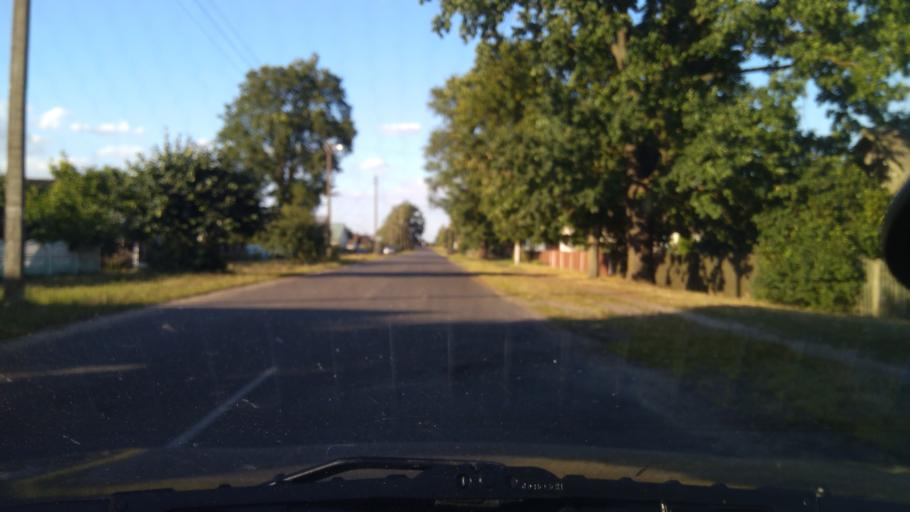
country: BY
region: Brest
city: Byaroza
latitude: 52.5856
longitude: 24.8658
